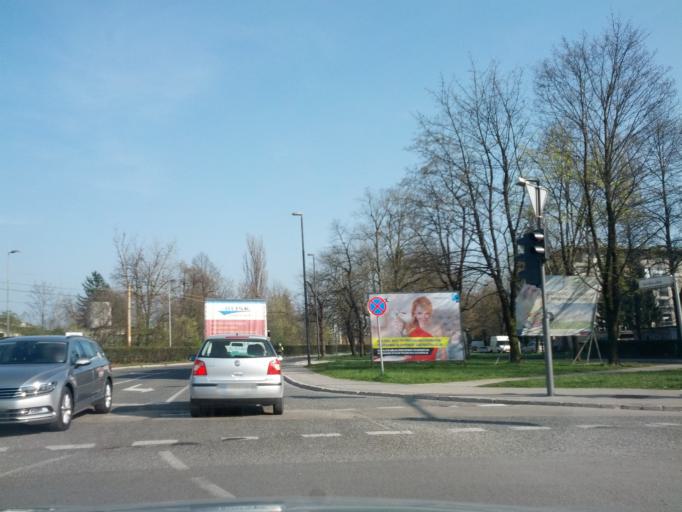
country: SI
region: Ljubljana
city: Ljubljana
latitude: 46.0773
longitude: 14.4891
